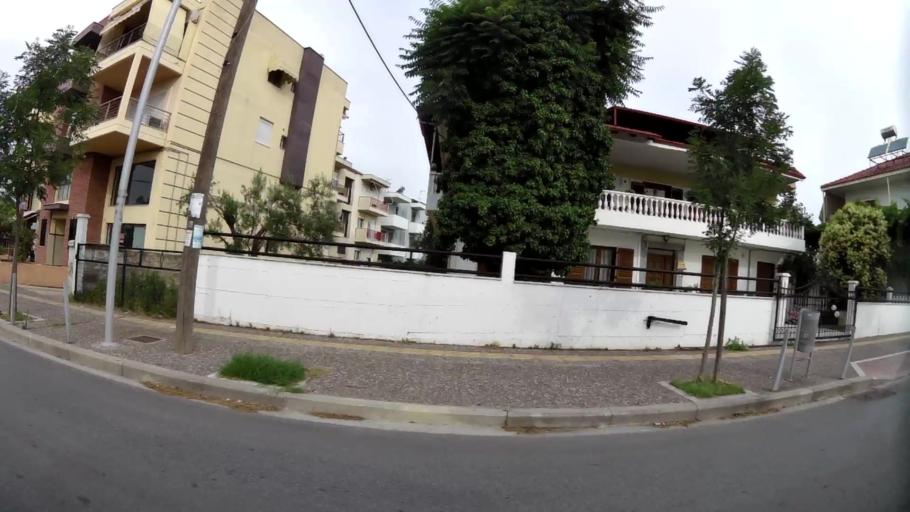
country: GR
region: Central Macedonia
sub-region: Nomos Thessalonikis
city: Thermi
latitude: 40.5435
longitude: 23.0190
